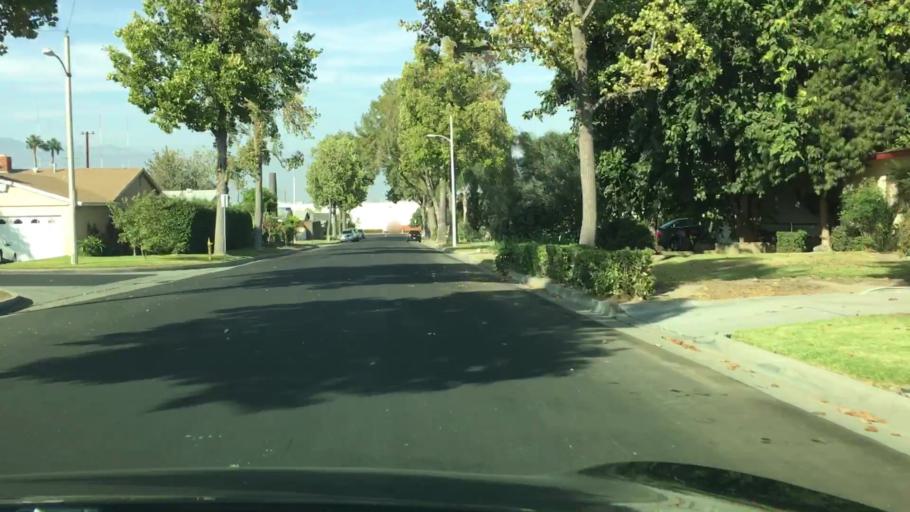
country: US
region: California
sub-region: Los Angeles County
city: Avocado Heights
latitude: 34.0212
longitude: -117.9858
